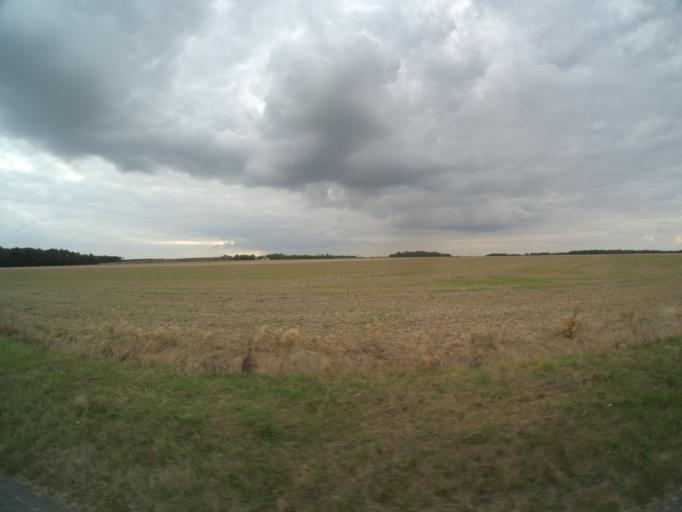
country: FR
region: Centre
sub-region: Departement d'Indre-et-Loire
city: Auzouer-en-Touraine
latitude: 47.4932
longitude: 0.9467
